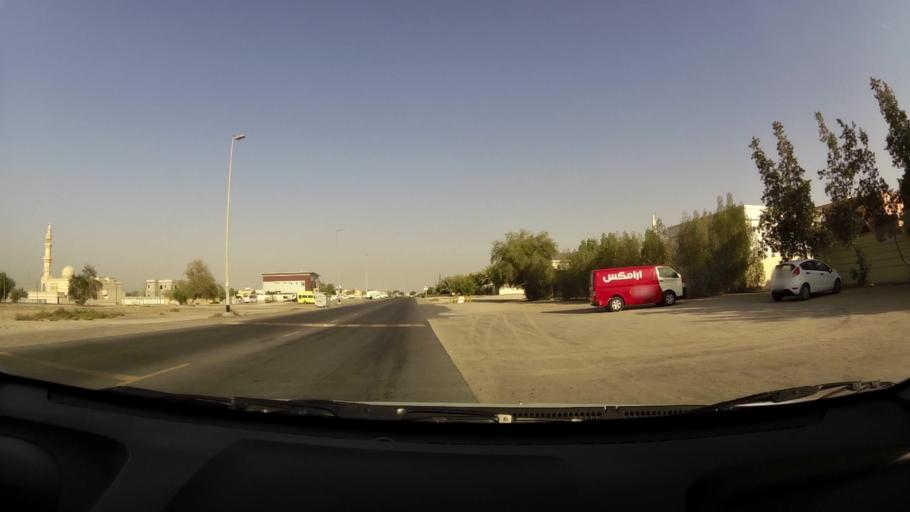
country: AE
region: Ash Shariqah
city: Sharjah
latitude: 25.2703
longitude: 55.3854
